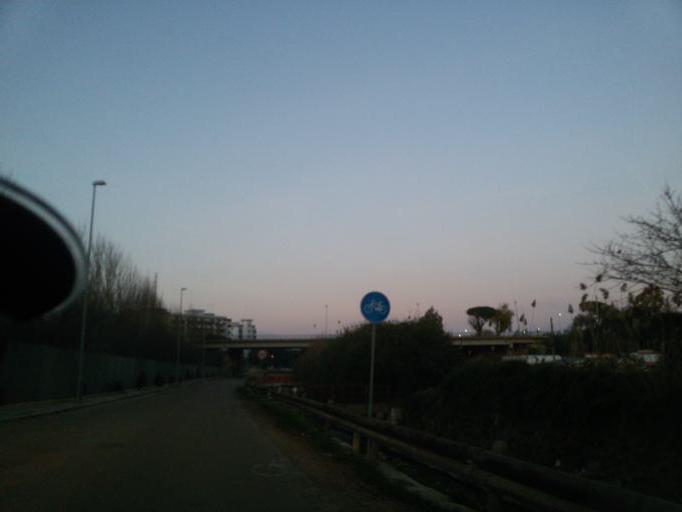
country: IT
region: Apulia
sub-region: Provincia di Brindisi
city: Brindisi
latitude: 40.6268
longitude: 17.9392
